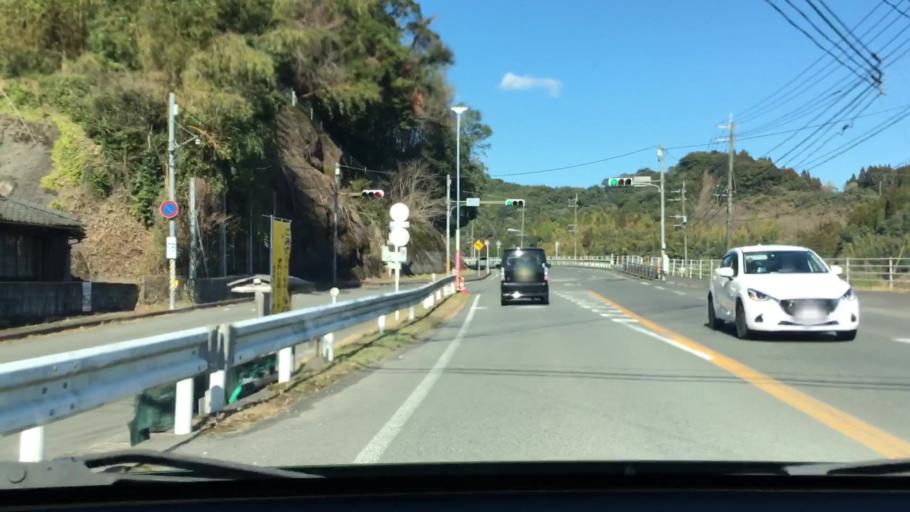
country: JP
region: Kagoshima
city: Ijuin
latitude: 31.6574
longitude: 130.4960
